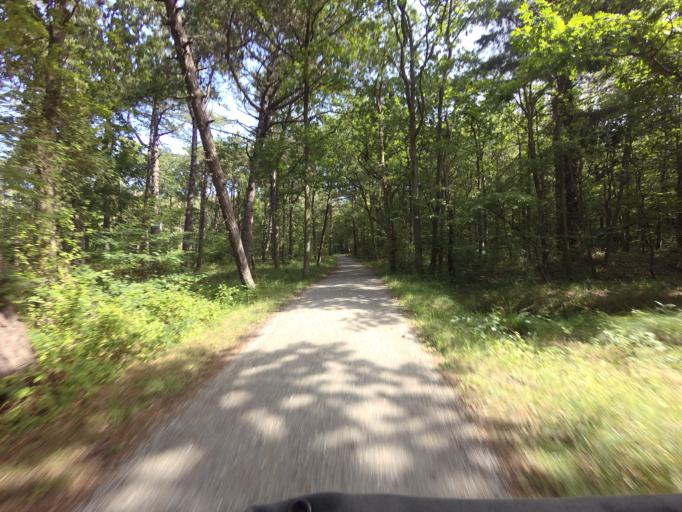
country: NL
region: Friesland
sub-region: Gemeente Terschelling
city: West-Terschelling
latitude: 53.3758
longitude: 5.2052
